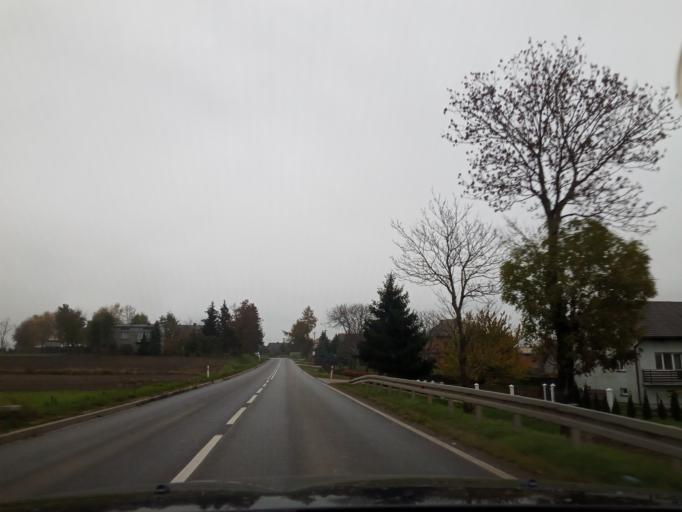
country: PL
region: Lesser Poland Voivodeship
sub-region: Powiat proszowicki
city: Klimontow
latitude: 50.2135
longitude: 20.3123
